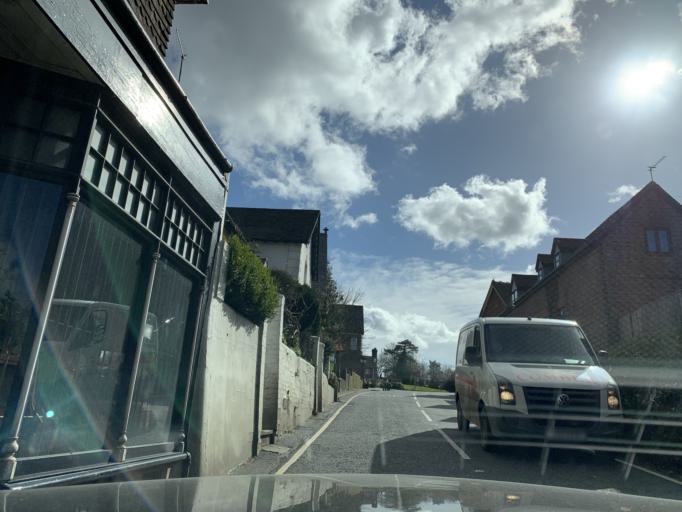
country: GB
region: England
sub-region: West Sussex
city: Crawley Down
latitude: 51.1046
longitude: -0.0851
